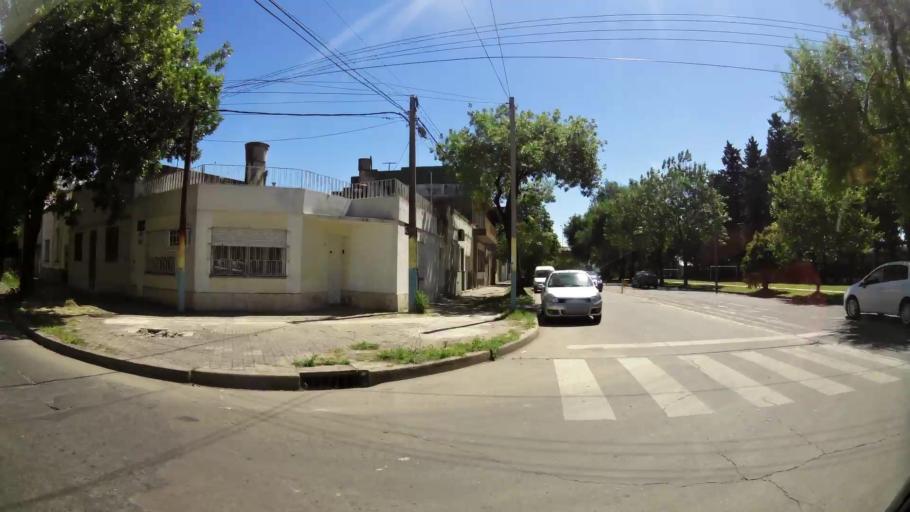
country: AR
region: Santa Fe
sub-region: Departamento de Rosario
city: Rosario
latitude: -32.9335
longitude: -60.6764
